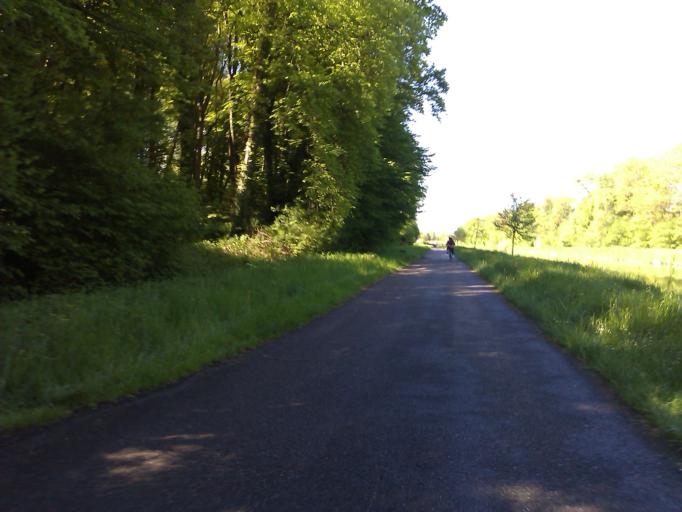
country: FR
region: Alsace
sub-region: Departement du Haut-Rhin
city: Dannemarie
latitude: 47.6582
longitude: 7.1669
